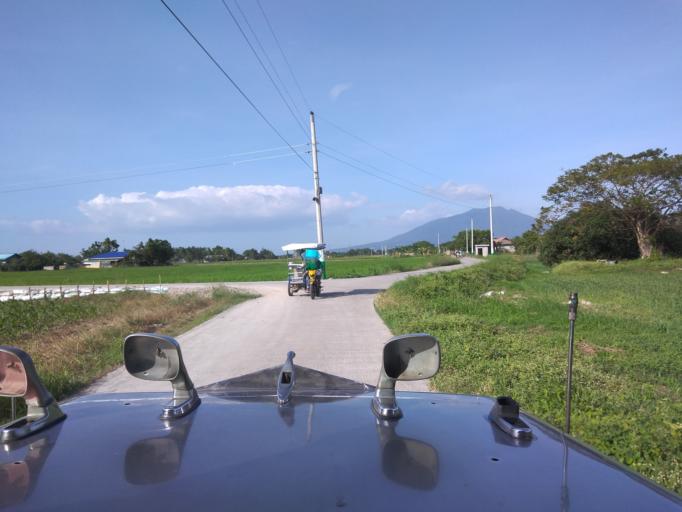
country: PH
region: Central Luzon
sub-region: Province of Pampanga
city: Bulaon
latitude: 15.0945
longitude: 120.6932
